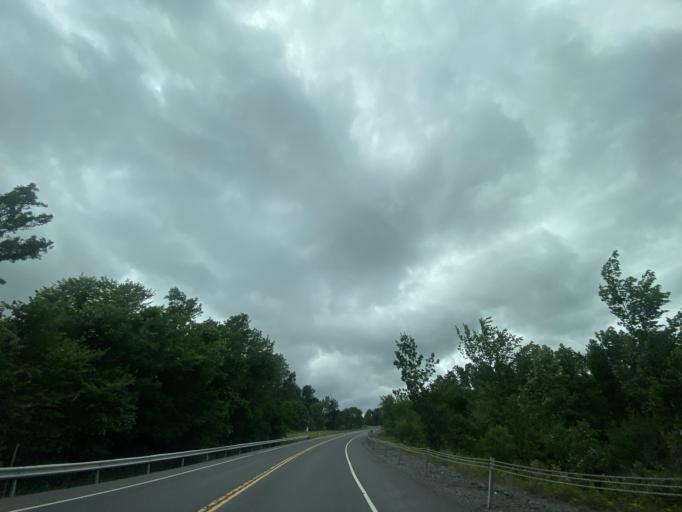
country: US
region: New York
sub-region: Greene County
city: Cairo
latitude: 42.3938
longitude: -73.9738
